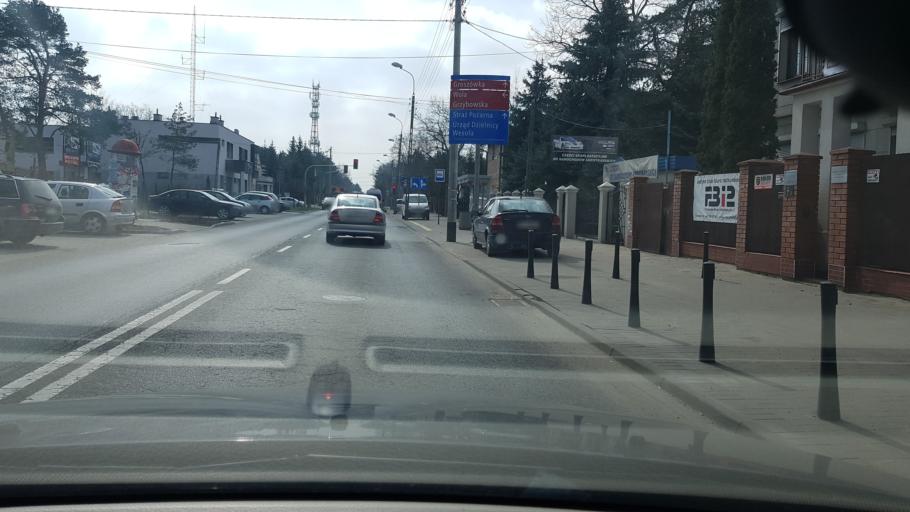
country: PL
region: Masovian Voivodeship
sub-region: Warszawa
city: Wesola
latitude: 52.2516
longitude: 21.2239
